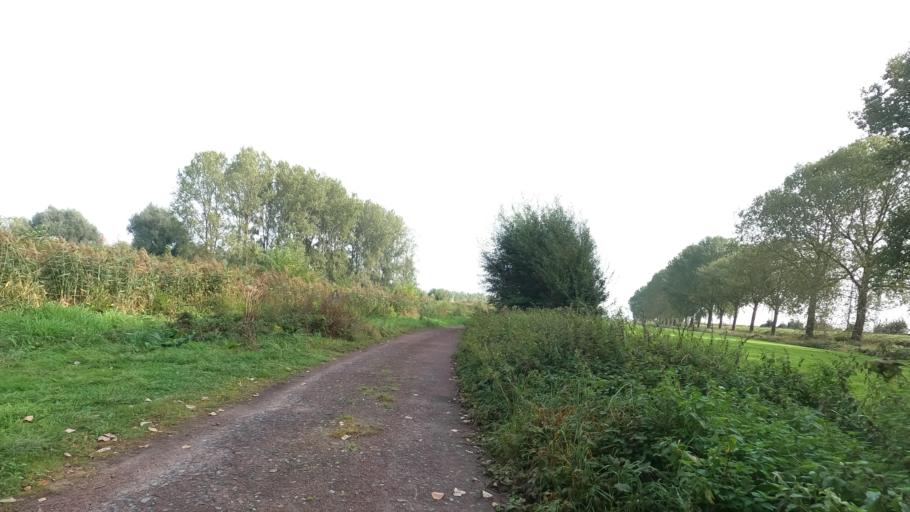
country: BE
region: Flanders
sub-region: Provincie Oost-Vlaanderen
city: Beveren
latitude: 51.2411
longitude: 4.2061
